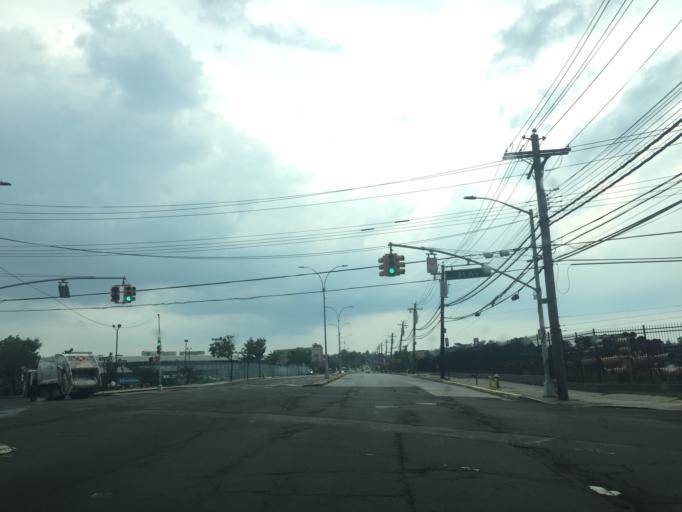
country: US
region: New York
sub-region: Bronx
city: The Bronx
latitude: 40.7691
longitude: -73.8414
